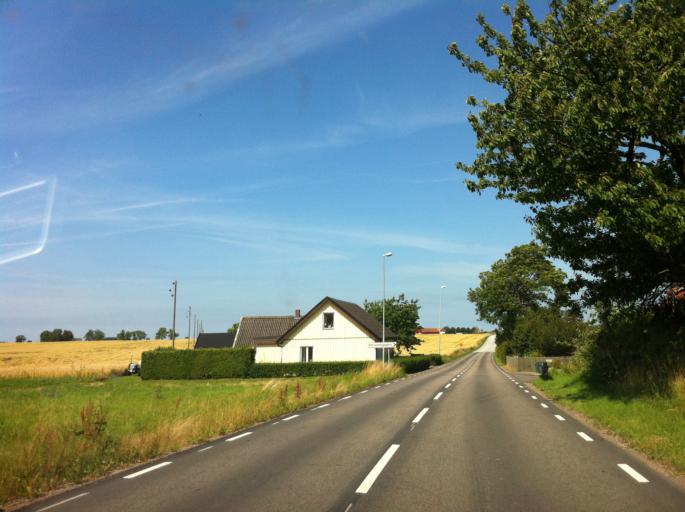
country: SE
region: Skane
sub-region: Helsingborg
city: Glumslov
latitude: 55.9671
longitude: 12.8294
